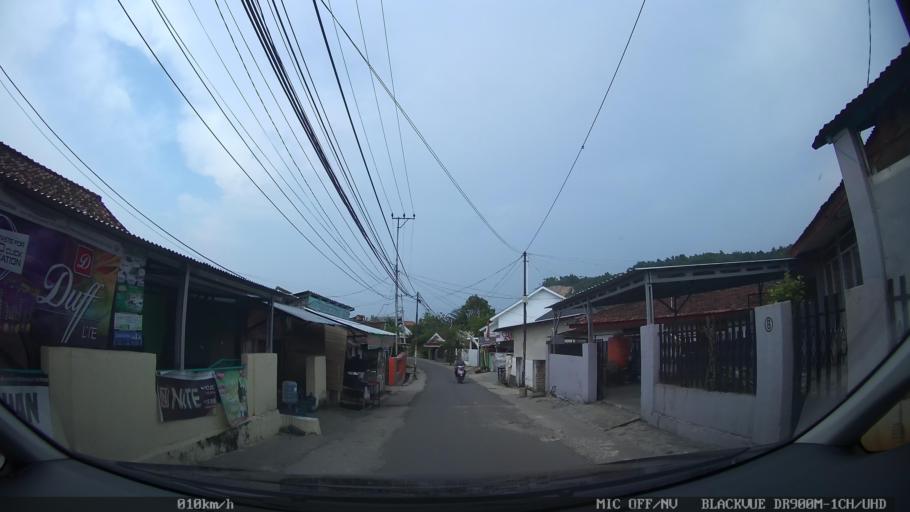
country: ID
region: Lampung
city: Bandarlampung
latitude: -5.4245
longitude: 105.2763
